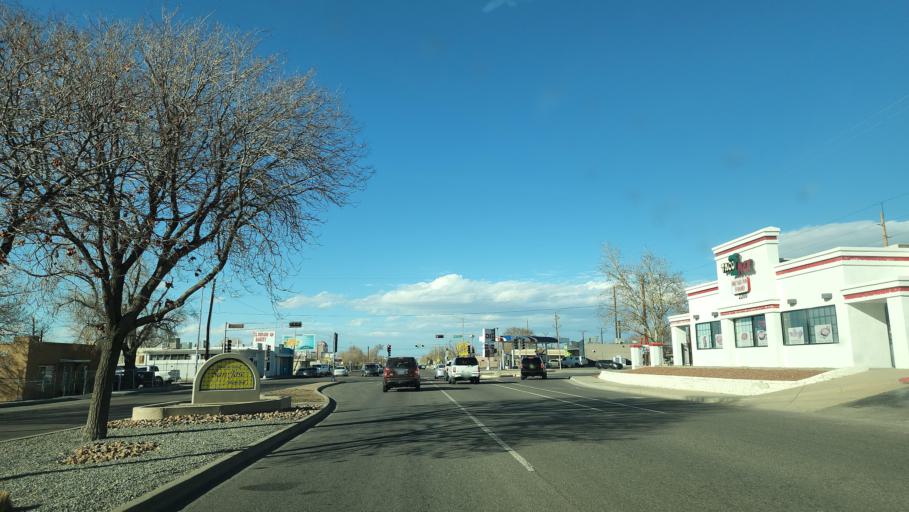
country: US
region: New Mexico
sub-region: Bernalillo County
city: Albuquerque
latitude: 35.0603
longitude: -106.6452
